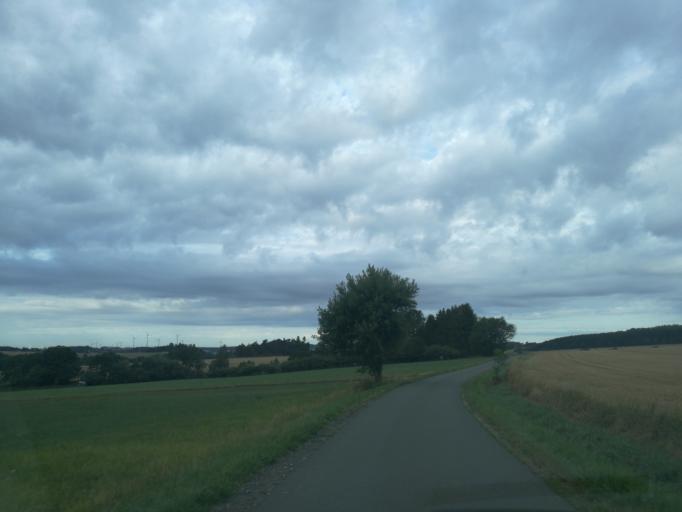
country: DE
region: Bavaria
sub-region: Upper Franconia
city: Regnitzlosau
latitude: 50.3232
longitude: 12.0944
